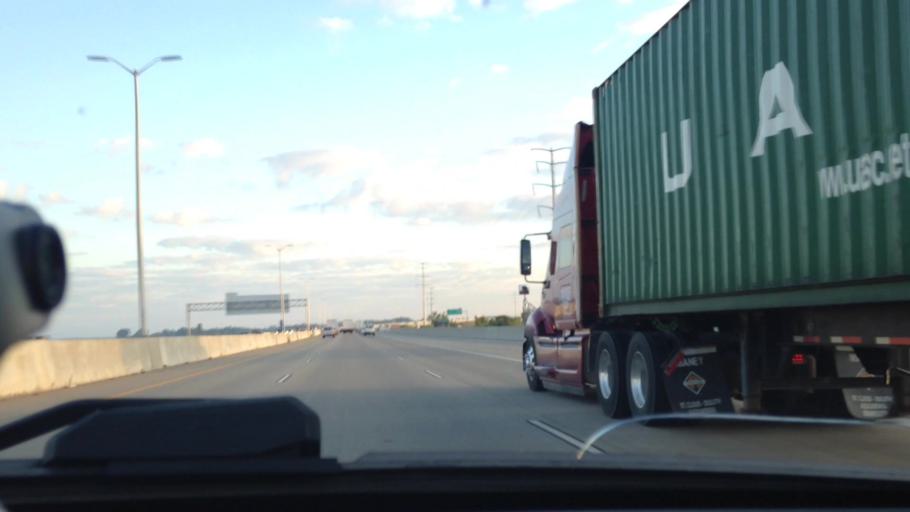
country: US
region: Wisconsin
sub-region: Winnebago County
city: Oshkosh
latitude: 44.0362
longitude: -88.5829
